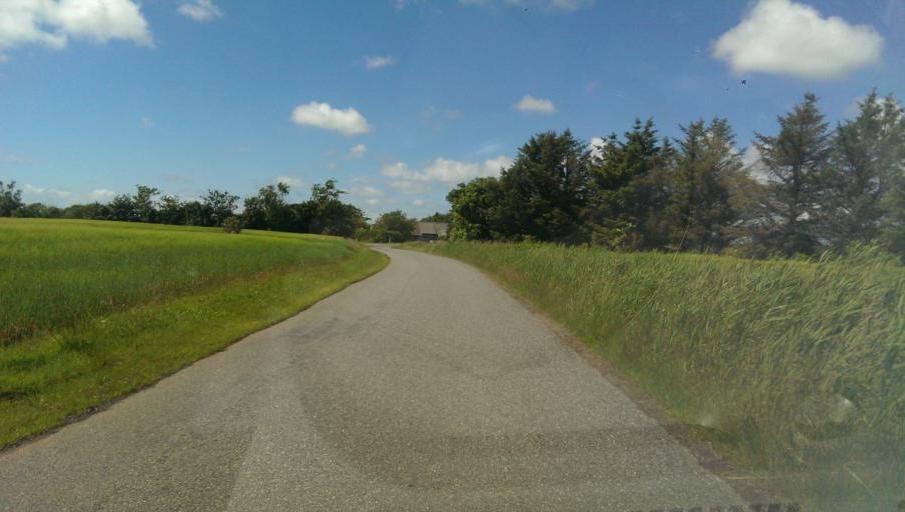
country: DK
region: Central Jutland
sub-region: Holstebro Kommune
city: Ulfborg
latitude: 56.2471
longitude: 8.2335
